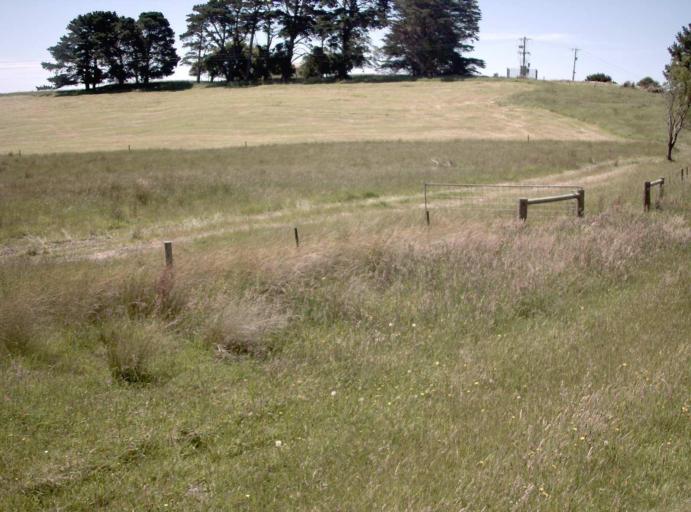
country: AU
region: Victoria
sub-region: Latrobe
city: Morwell
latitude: -38.6879
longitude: 146.1467
